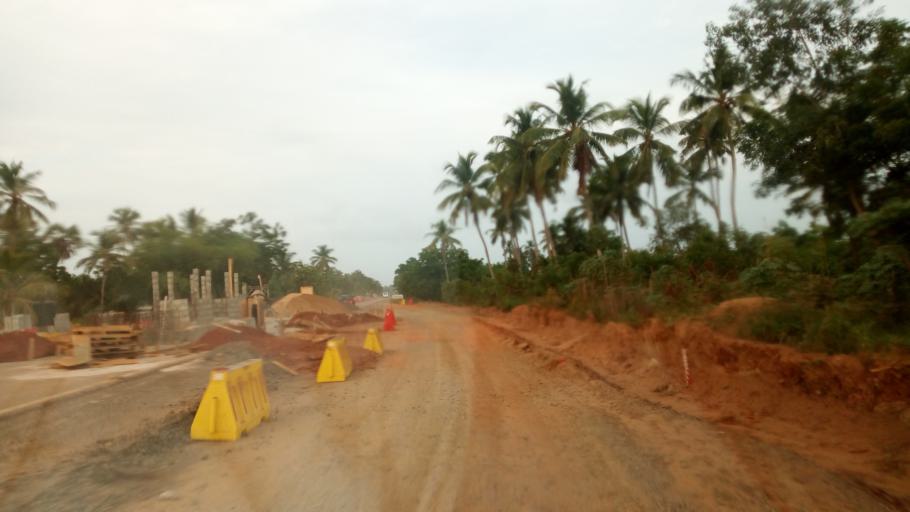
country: TG
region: Maritime
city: Lome
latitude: 6.0893
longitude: 1.0668
